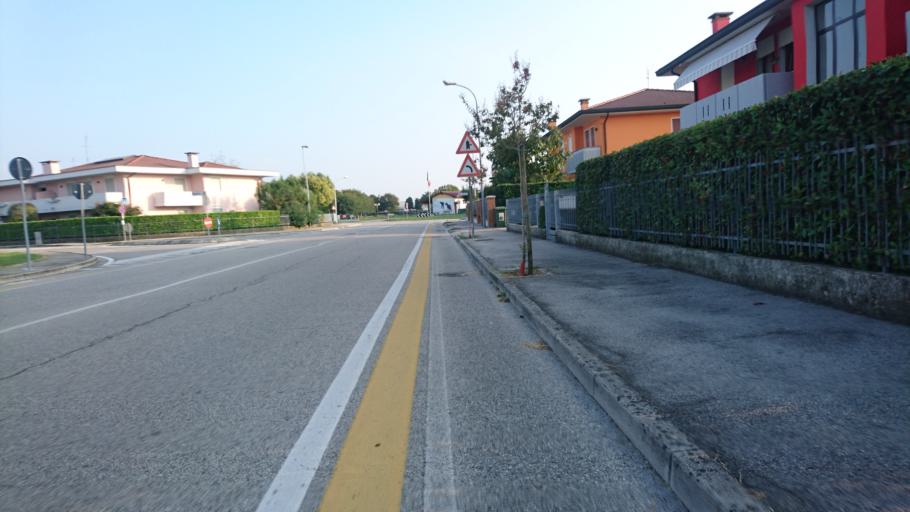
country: IT
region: Veneto
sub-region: Provincia di Padova
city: Limena
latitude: 45.4706
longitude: 11.8439
